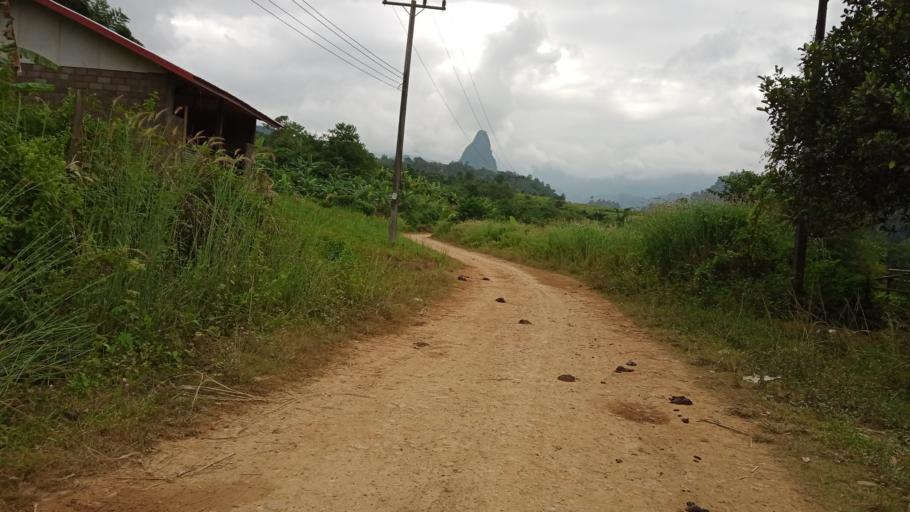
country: LA
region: Xiangkhoang
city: Phonsavan
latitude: 19.0922
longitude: 103.0045
